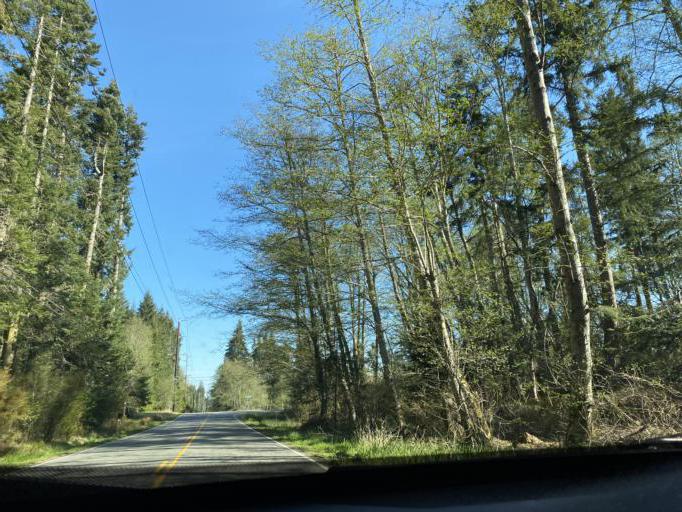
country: US
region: Washington
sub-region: Island County
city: Freeland
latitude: 48.0863
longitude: -122.5830
